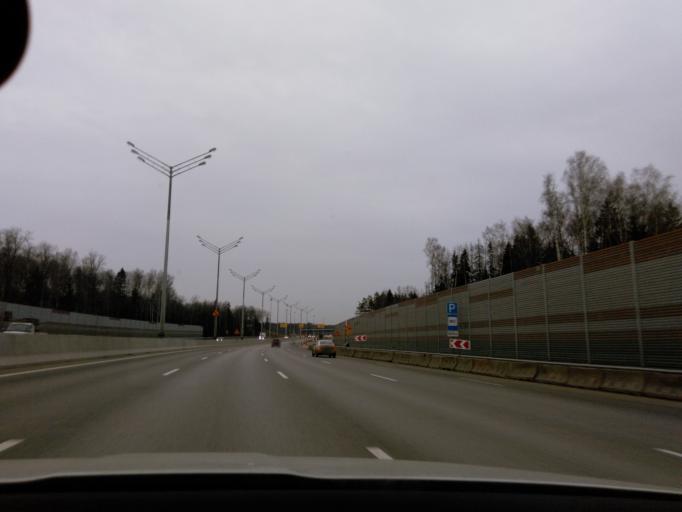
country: RU
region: Moscow
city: Khimki
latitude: 55.9423
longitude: 37.4479
